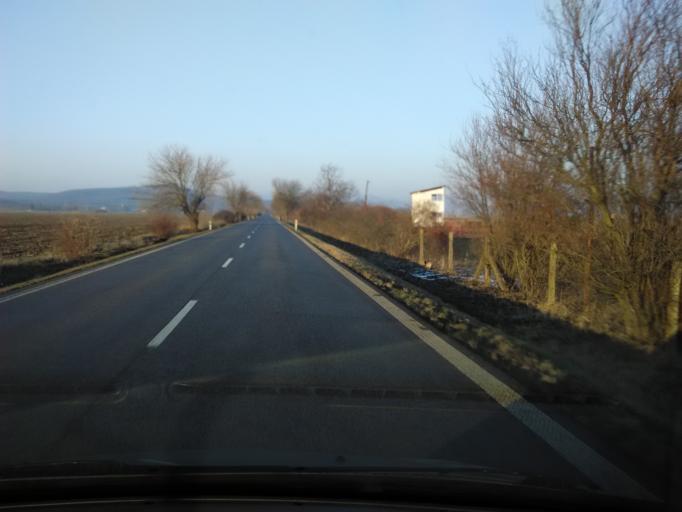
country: SK
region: Nitriansky
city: Tlmace
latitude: 48.2563
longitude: 18.5128
